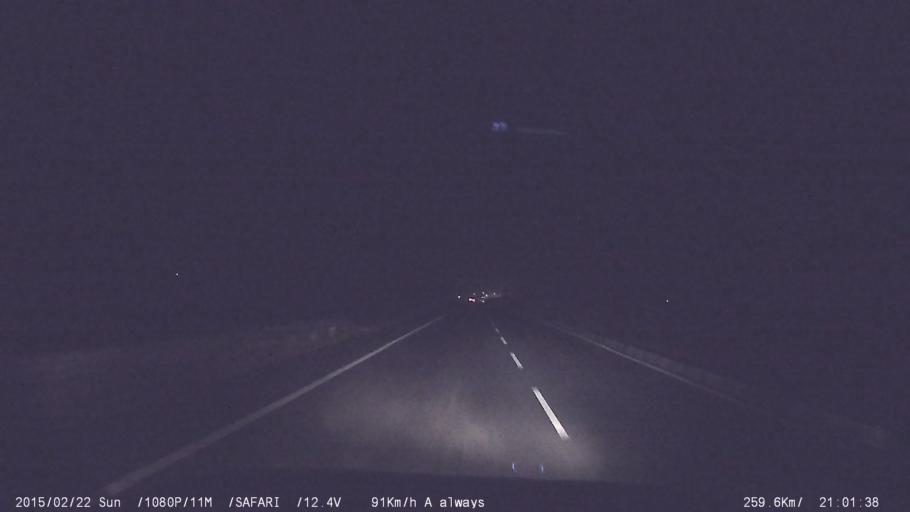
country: IN
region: Tamil Nadu
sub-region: Karur
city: Pallappatti
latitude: 10.6669
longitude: 77.9328
